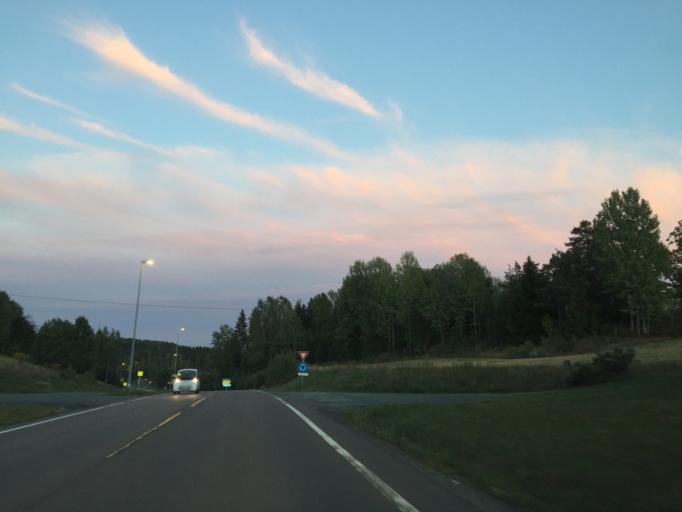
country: NO
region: Akershus
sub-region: Vestby
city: Vestby
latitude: 59.5180
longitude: 10.7186
